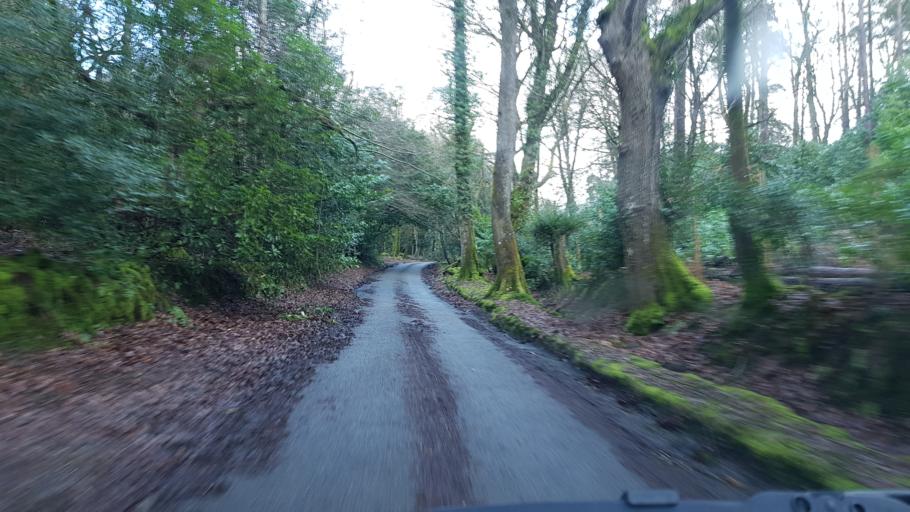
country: GB
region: England
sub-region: Surrey
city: Churt
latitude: 51.1076
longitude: -0.7710
